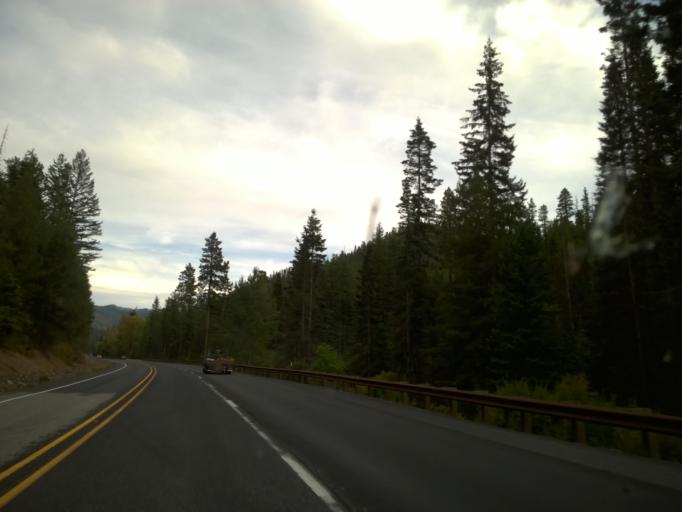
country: US
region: Washington
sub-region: Chelan County
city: Cashmere
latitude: 47.3873
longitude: -120.6019
